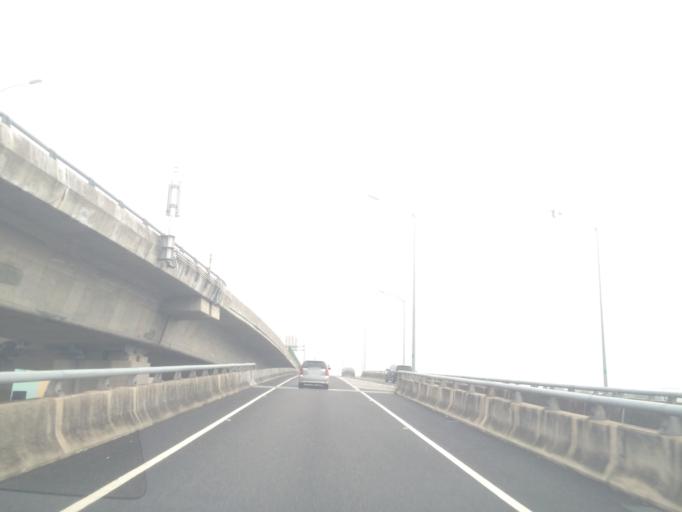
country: TW
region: Taiwan
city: Zhongxing New Village
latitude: 24.0264
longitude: 120.6703
